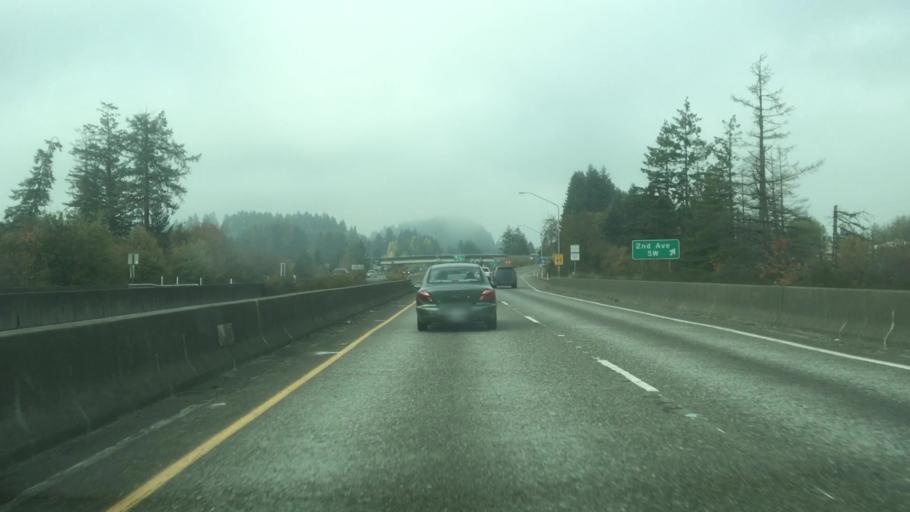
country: US
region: Washington
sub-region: Thurston County
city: Tumwater
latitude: 47.0449
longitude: -122.9904
